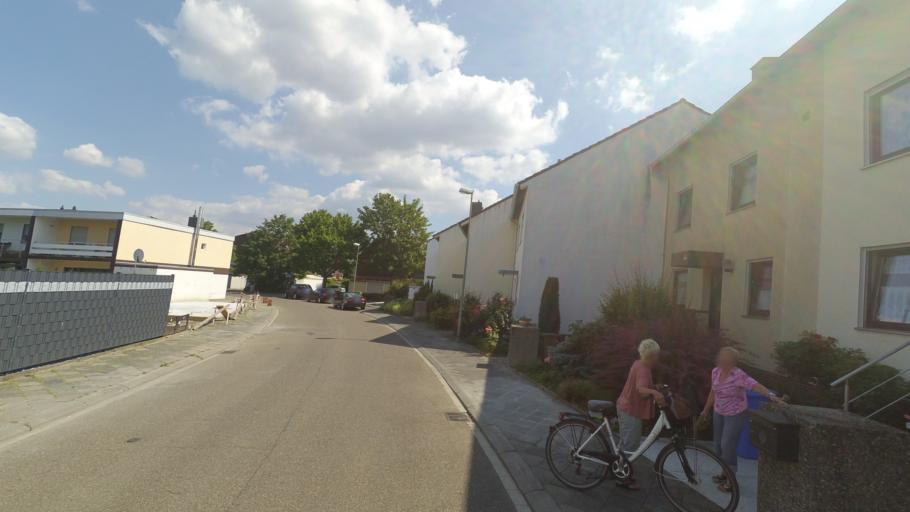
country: DE
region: Rheinland-Pfalz
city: Frankenthal
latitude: 49.5175
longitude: 8.3948
